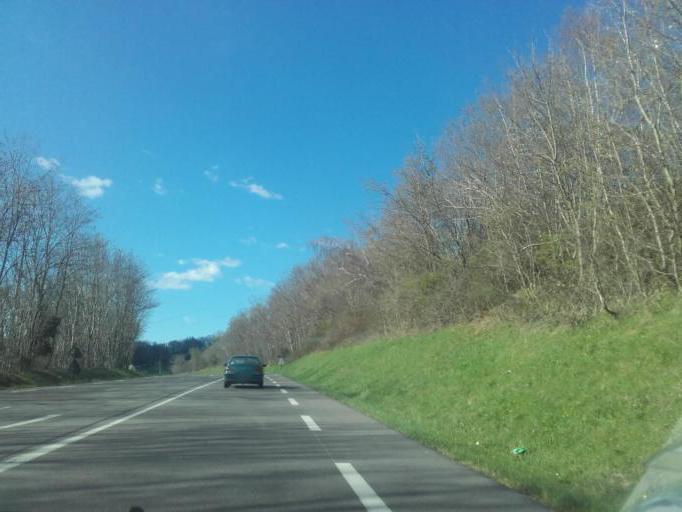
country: FR
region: Rhone-Alpes
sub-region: Departement de l'Isere
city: Saint-Hilaire-de-la-Cote
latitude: 45.4042
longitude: 5.3473
